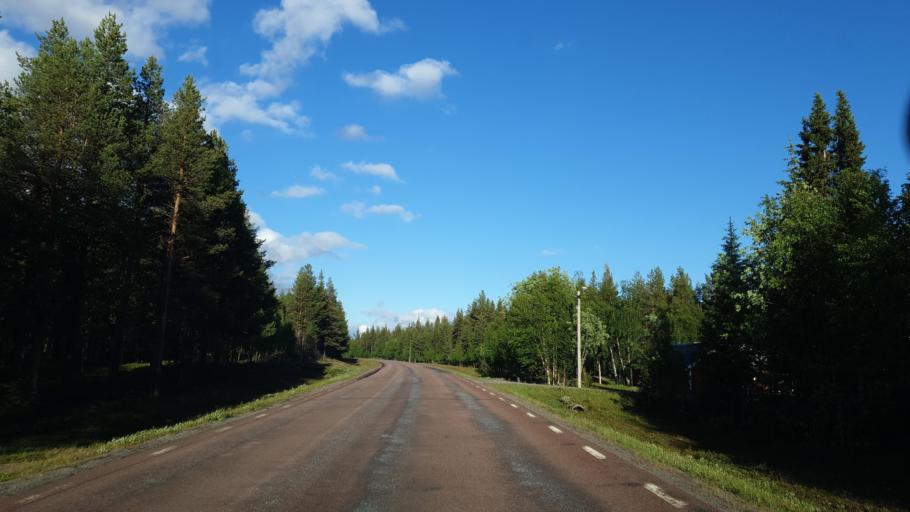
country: SE
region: Norrbotten
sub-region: Arjeplogs Kommun
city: Arjeplog
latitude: 66.0033
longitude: 18.1176
